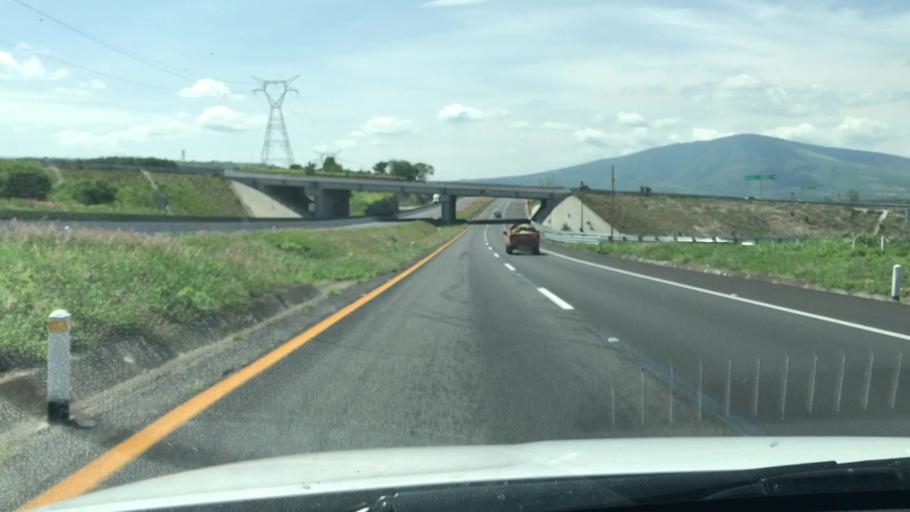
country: MX
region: Jalisco
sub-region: Zapotlanejo
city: La Mezquitera
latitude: 20.5875
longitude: -103.1007
